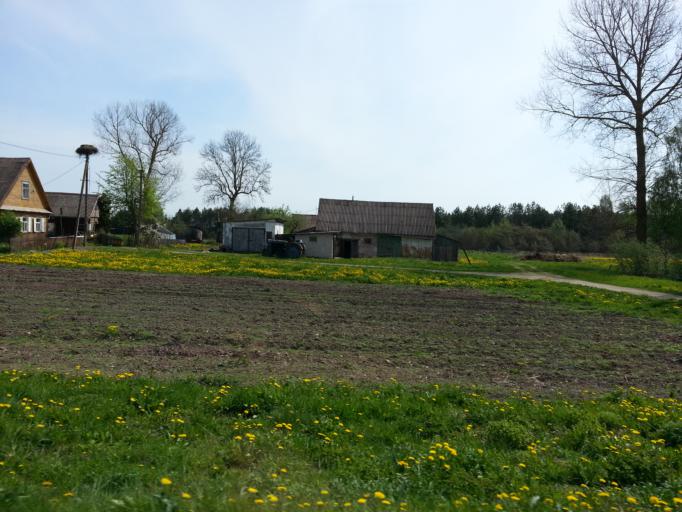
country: LT
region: Panevezys
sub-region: Panevezys City
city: Panevezys
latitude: 55.8847
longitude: 24.2329
